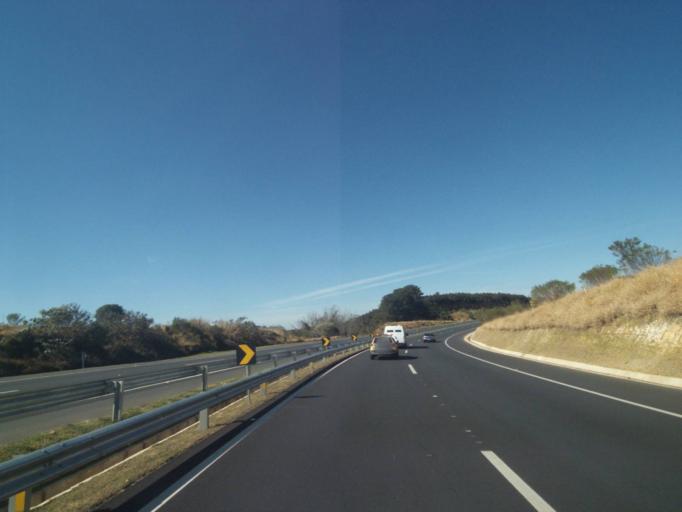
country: BR
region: Parana
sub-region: Tibagi
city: Tibagi
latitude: -24.8501
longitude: -50.4627
